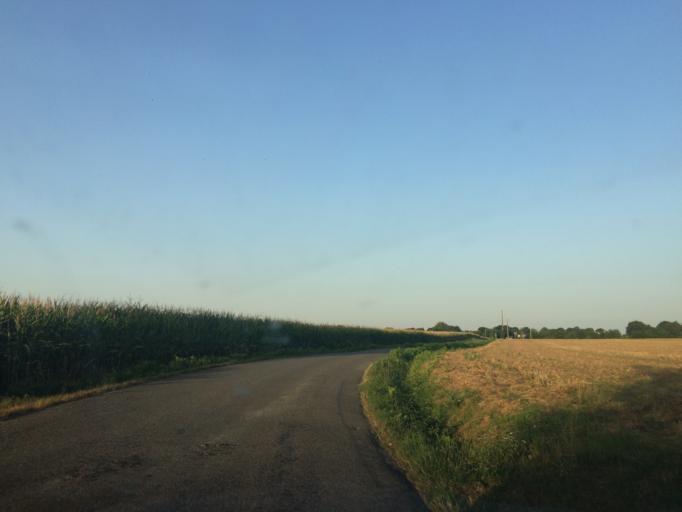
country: FR
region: Brittany
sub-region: Departement du Morbihan
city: Caden
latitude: 47.6365
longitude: -2.2502
